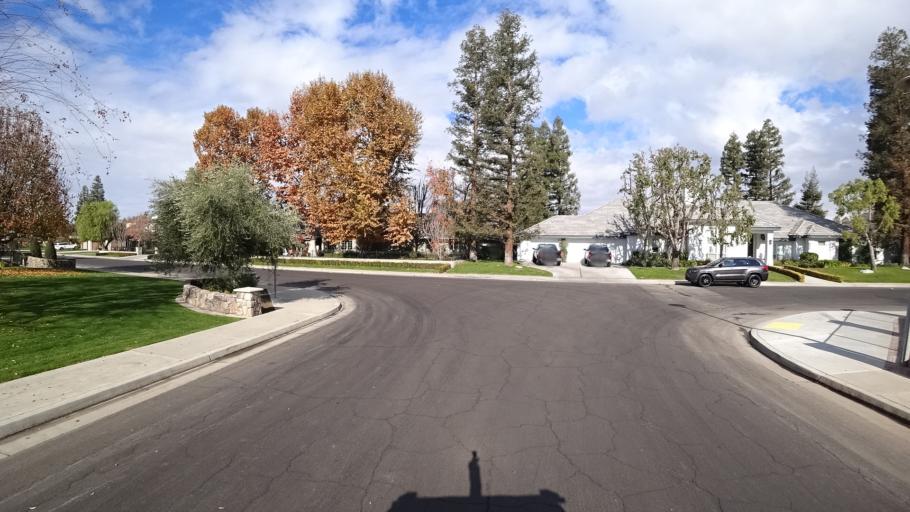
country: US
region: California
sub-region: Kern County
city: Greenacres
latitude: 35.3426
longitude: -119.0857
